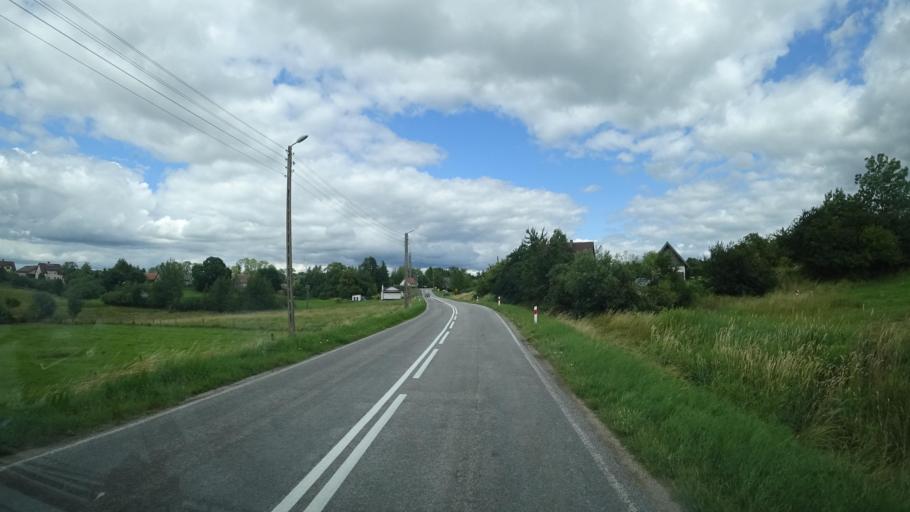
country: PL
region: Warmian-Masurian Voivodeship
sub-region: Powiat goldapski
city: Goldap
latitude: 54.2221
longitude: 22.2328
